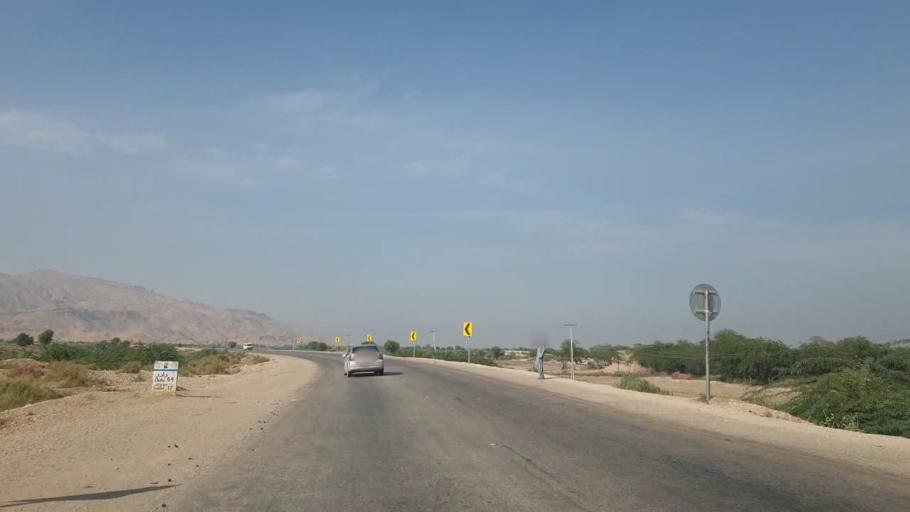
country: PK
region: Sindh
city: Sehwan
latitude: 26.2676
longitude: 67.9037
